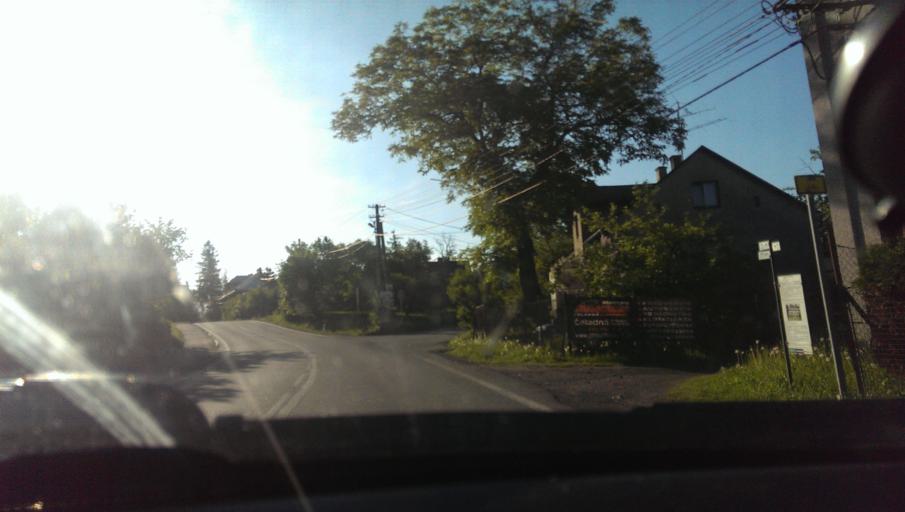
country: CZ
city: Kuncice pod Ondrejnikem
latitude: 49.5386
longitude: 18.2989
